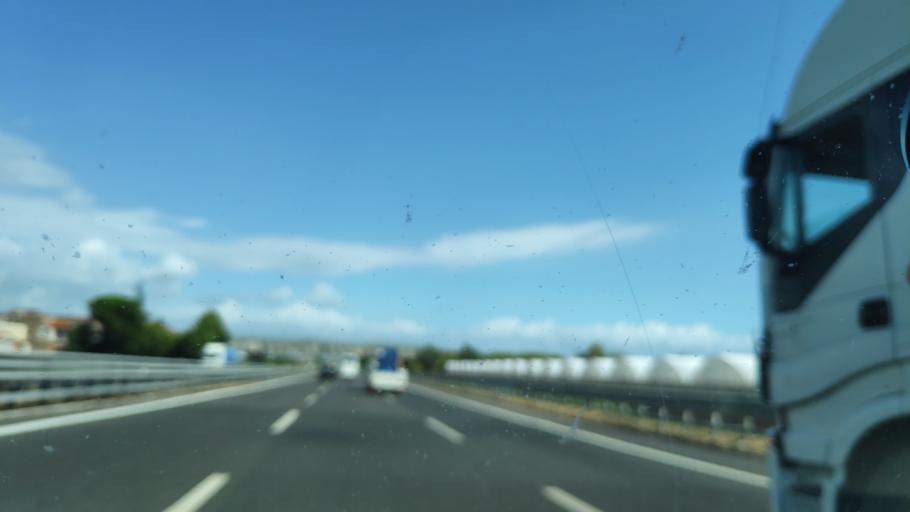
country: IT
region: Campania
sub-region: Provincia di Salerno
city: Sant'Antonio
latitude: 40.6436
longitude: 14.8938
